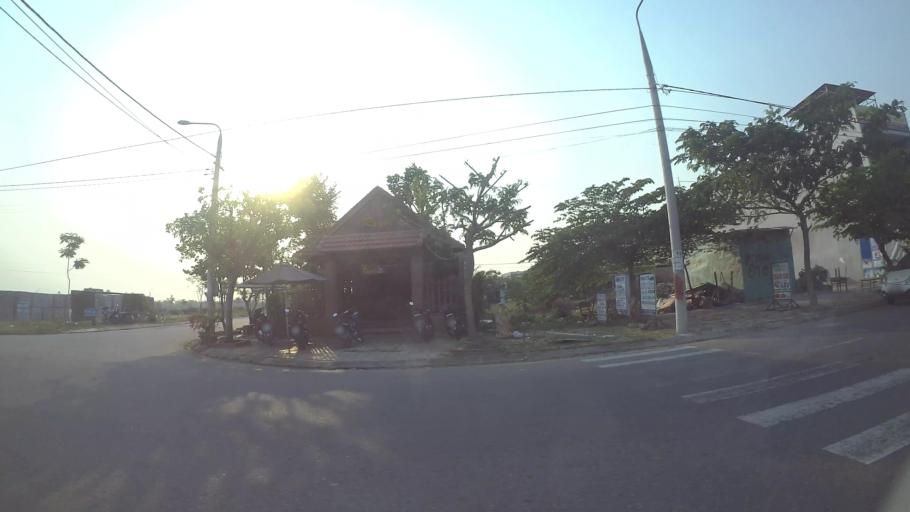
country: VN
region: Da Nang
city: Ngu Hanh Son
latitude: 15.9786
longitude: 108.2337
